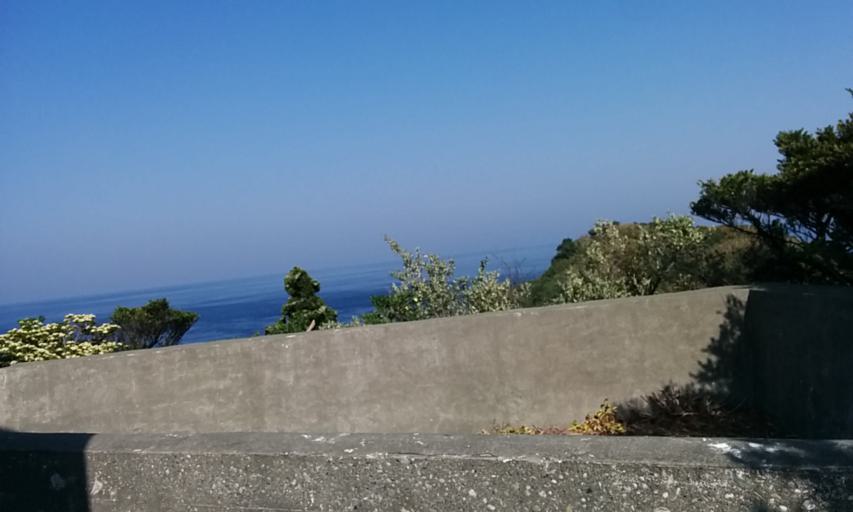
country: JP
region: Oita
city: Usuki
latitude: 33.3432
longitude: 132.0150
